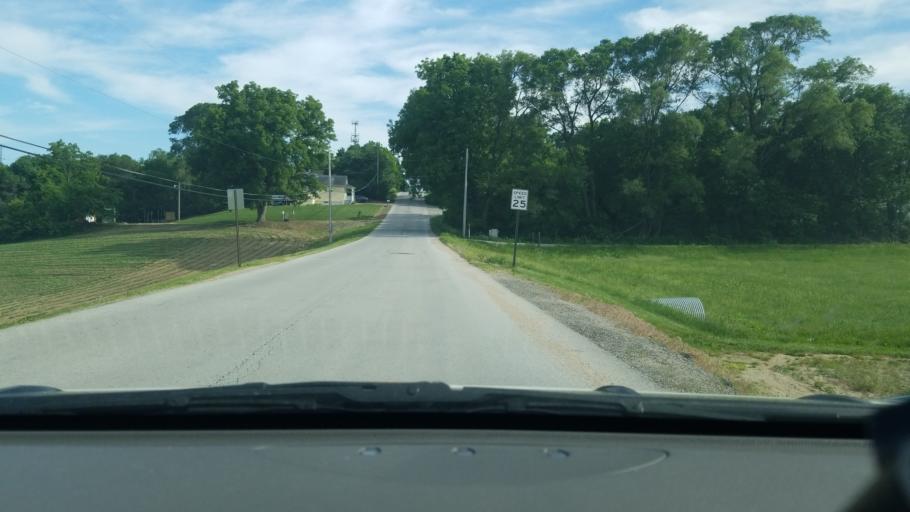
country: US
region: Nebraska
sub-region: Sarpy County
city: Offutt Air Force Base
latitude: 41.1723
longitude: -95.9336
